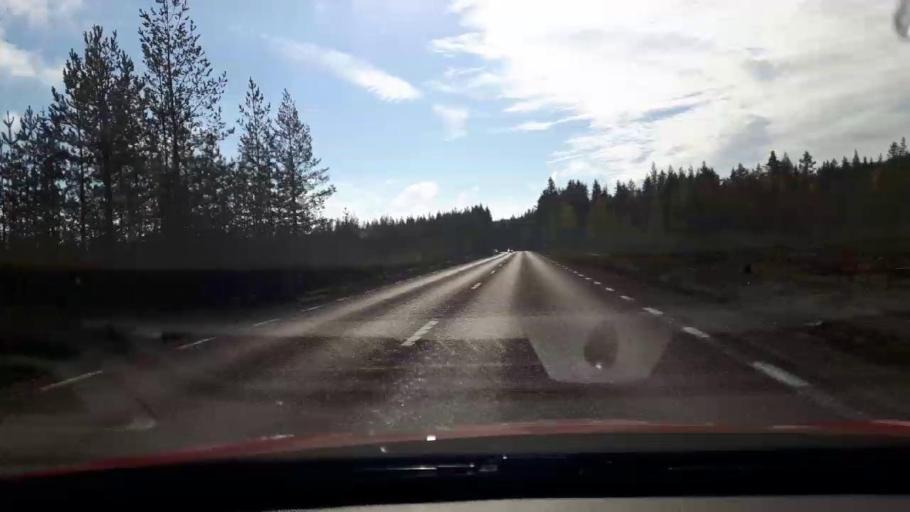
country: SE
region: Gaevleborg
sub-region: Ljusdals Kommun
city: Farila
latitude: 61.9104
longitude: 15.6283
